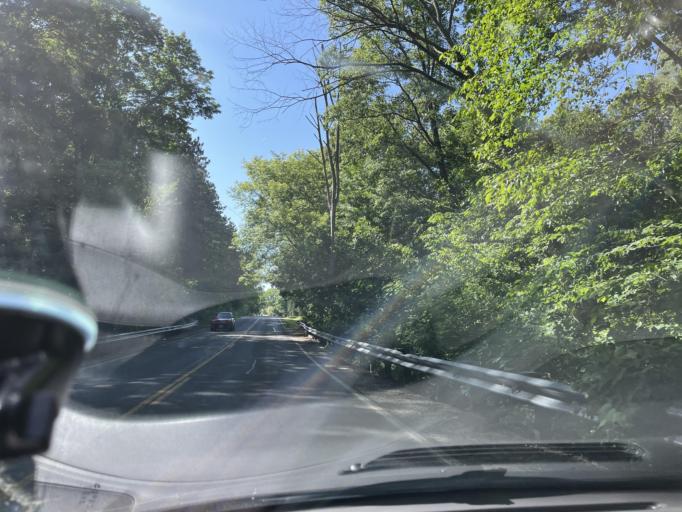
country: US
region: Michigan
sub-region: Barry County
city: Hastings
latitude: 42.6486
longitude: -85.3251
